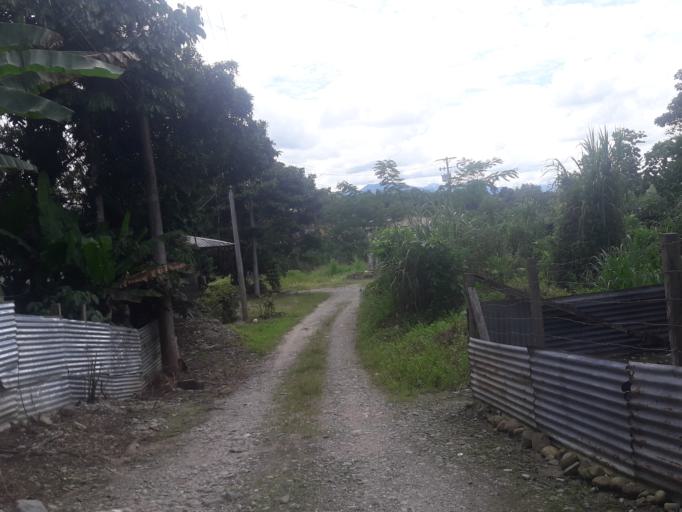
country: EC
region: Napo
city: Tena
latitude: -0.9923
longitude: -77.8088
